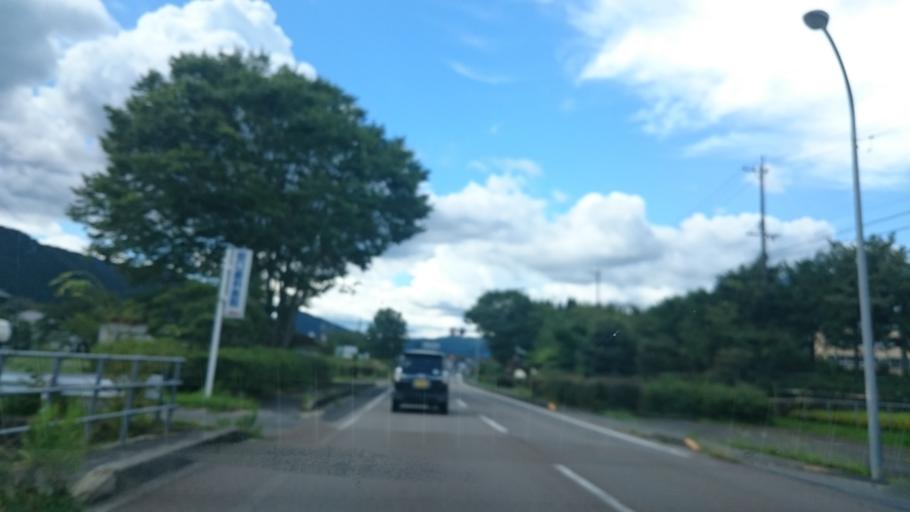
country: JP
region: Gifu
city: Nakatsugawa
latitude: 35.6410
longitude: 137.4434
